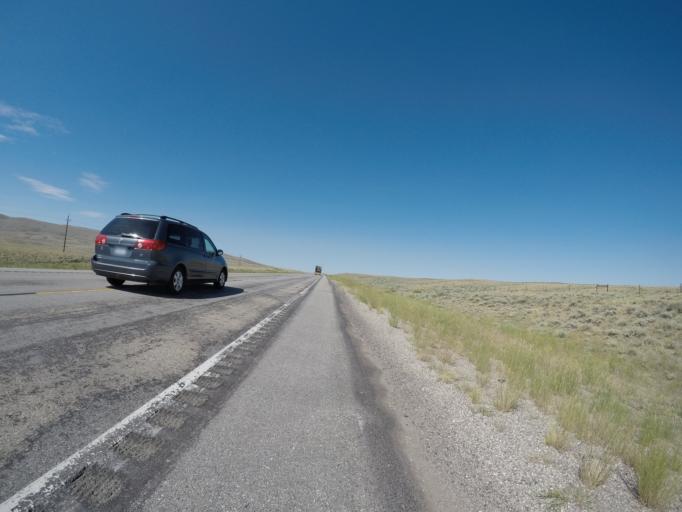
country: US
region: Wyoming
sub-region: Carbon County
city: Saratoga
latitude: 41.8013
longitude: -106.7084
